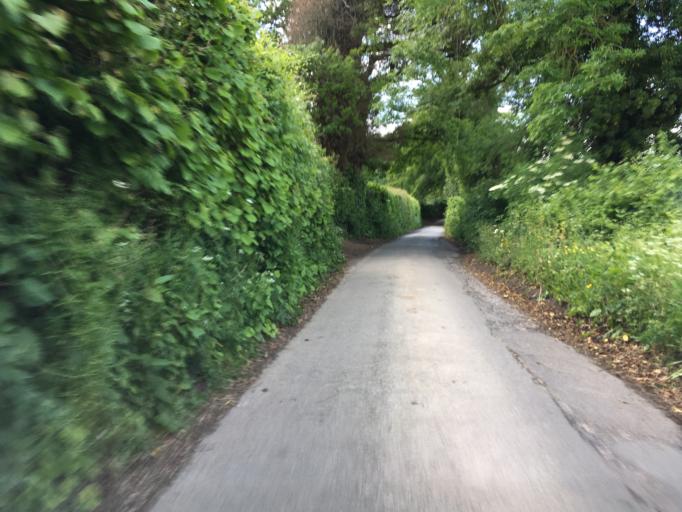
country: GB
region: England
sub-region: Gloucestershire
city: Painswick
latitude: 51.7756
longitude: -2.1867
